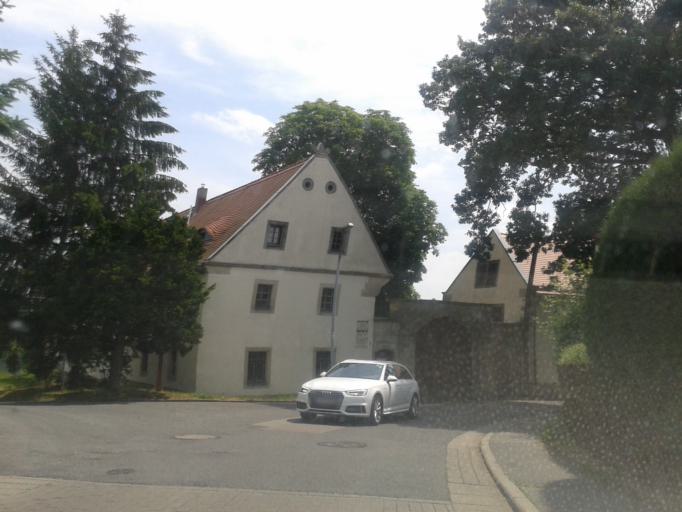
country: DE
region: Saxony
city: Bannewitz
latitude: 50.9949
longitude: 13.7245
